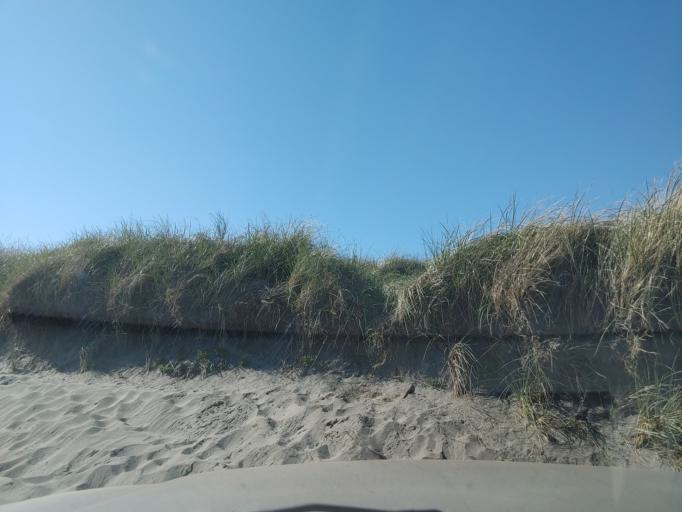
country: US
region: Oregon
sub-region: Clatsop County
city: Warrenton
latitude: 46.1784
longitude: -123.9788
